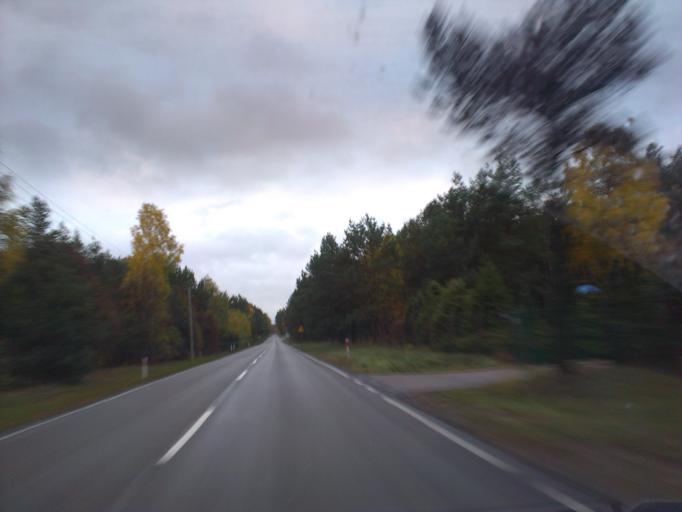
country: PL
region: Kujawsko-Pomorskie
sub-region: Powiat tucholski
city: Cekcyn
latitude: 53.5271
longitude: 17.9477
